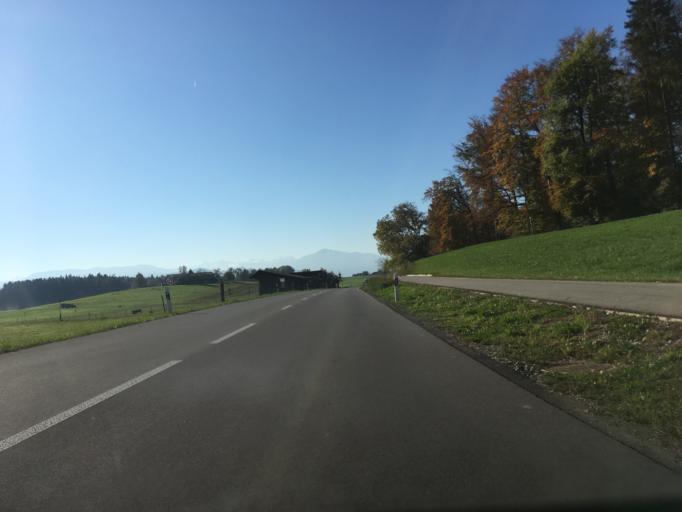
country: CH
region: Zurich
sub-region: Bezirk Affoltern
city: Hausen am Albis / Hausen (Dorf)
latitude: 47.2406
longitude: 8.5317
